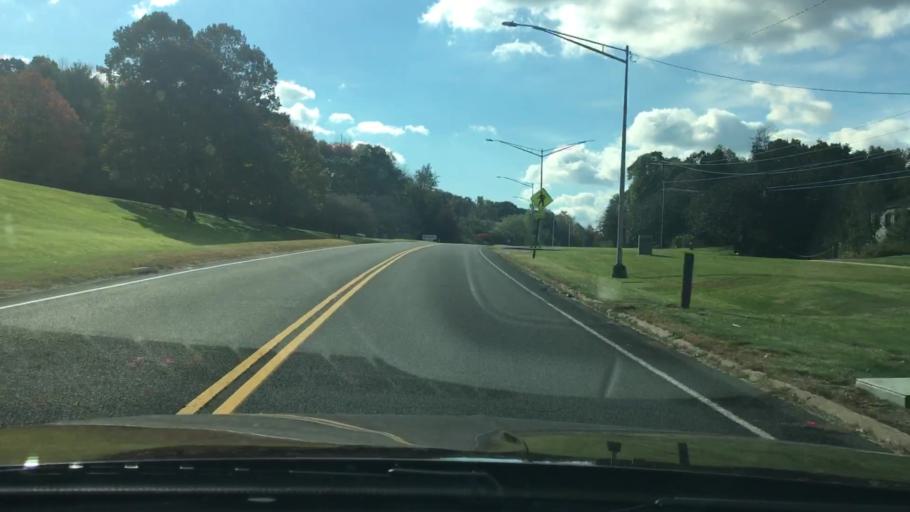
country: US
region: Connecticut
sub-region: New Haven County
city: Meriden
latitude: 41.5026
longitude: -72.7646
